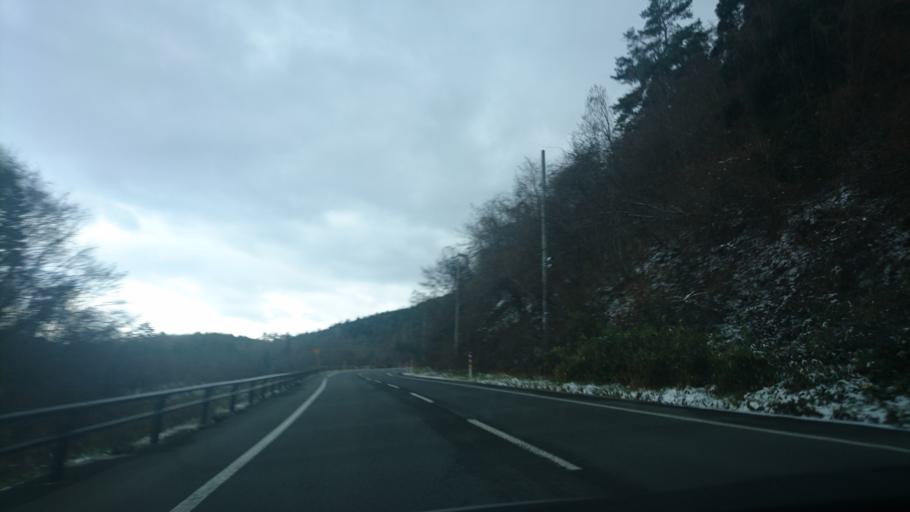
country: JP
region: Iwate
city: Mizusawa
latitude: 39.1641
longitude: 141.2506
